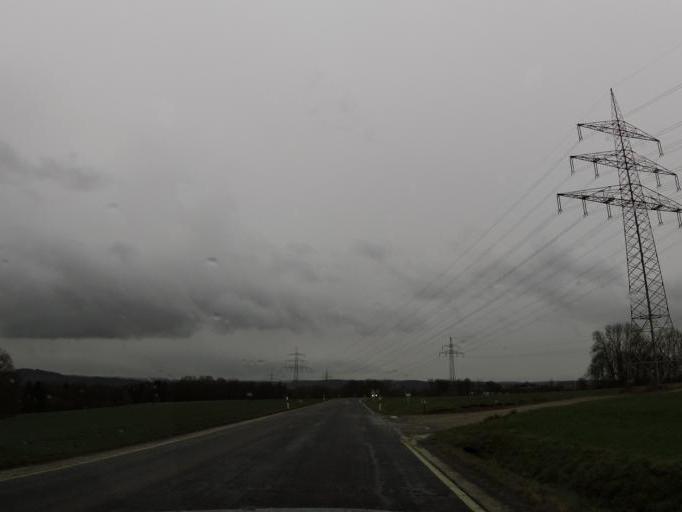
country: DE
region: Bavaria
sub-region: Regierungsbezirk Unterfranken
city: Marktheidenfeld
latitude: 49.8135
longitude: 9.5781
